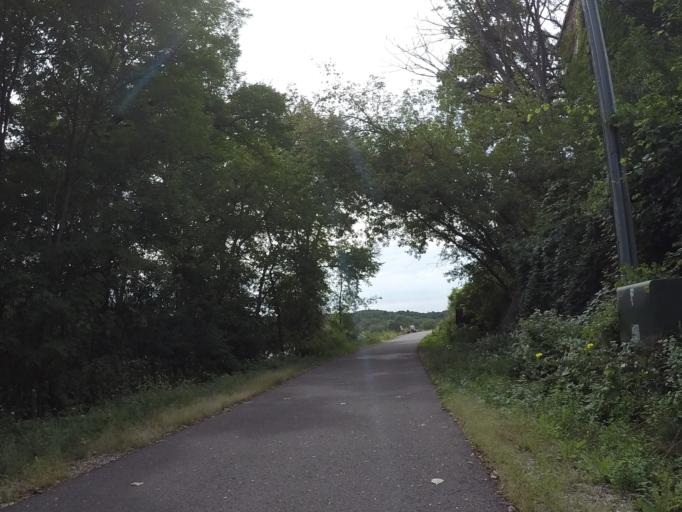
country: US
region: Wisconsin
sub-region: Sauk County
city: Prairie du Sac
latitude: 43.2920
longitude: -89.7212
